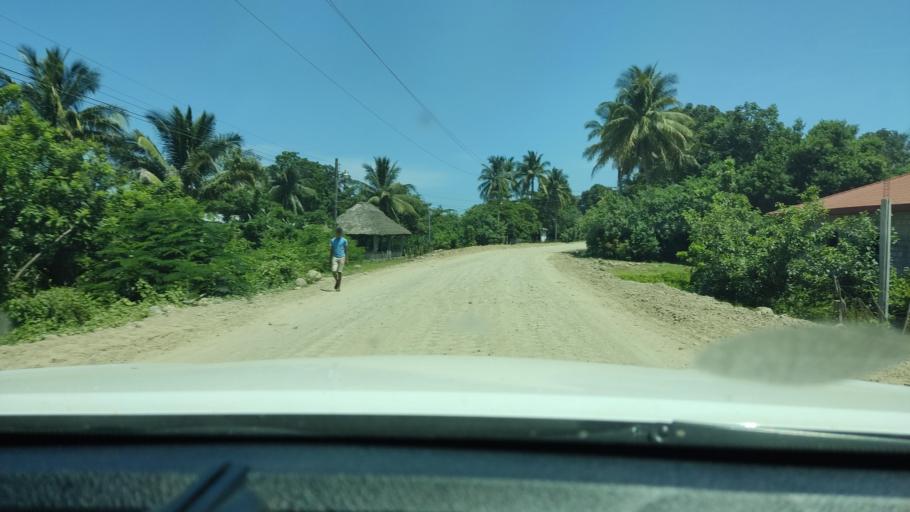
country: SV
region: Ahuachapan
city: San Francisco Menendez
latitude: 13.7746
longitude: -90.1128
